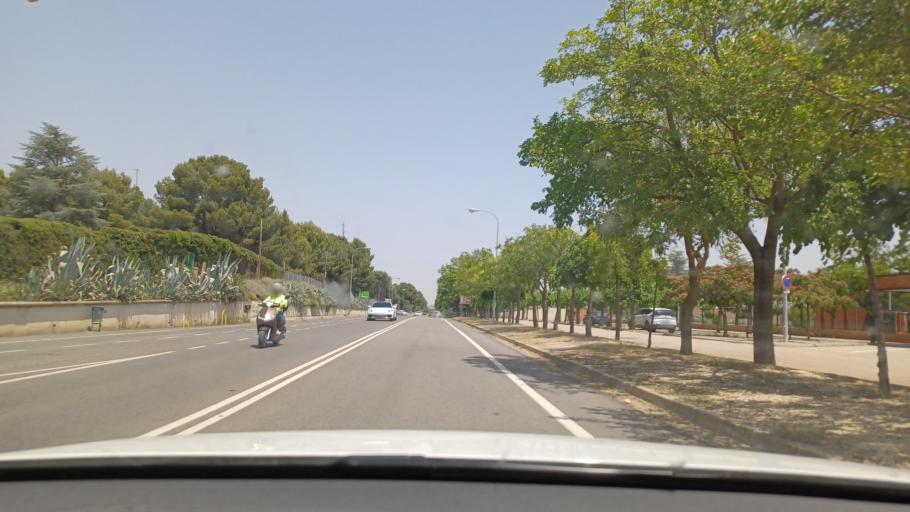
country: ES
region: Navarre
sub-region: Provincia de Navarra
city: Tudela
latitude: 42.0489
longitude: -1.6154
